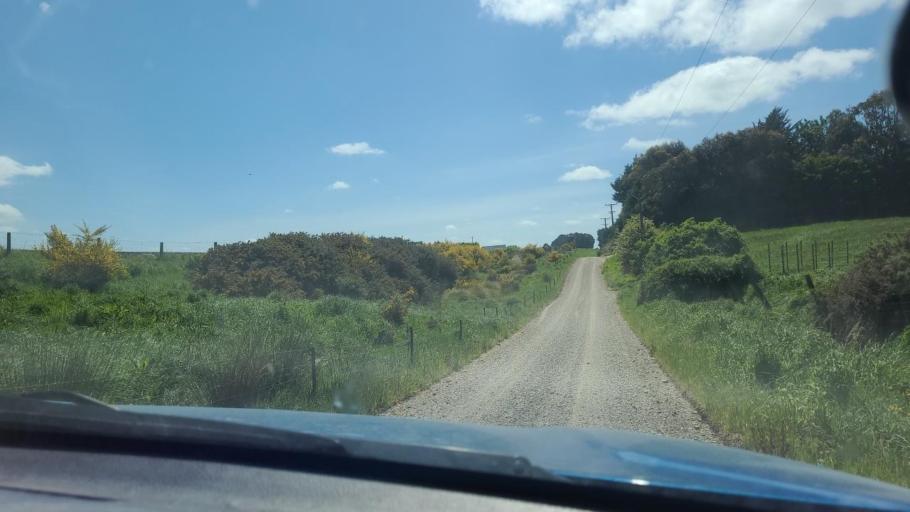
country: NZ
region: Southland
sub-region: Invercargill City
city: Invercargill
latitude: -46.3247
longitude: 168.3406
